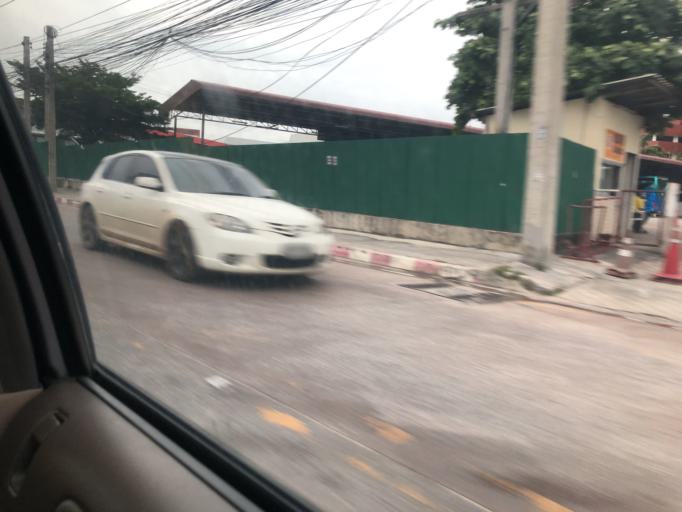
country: TH
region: Chon Buri
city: Phatthaya
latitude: 12.9485
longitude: 100.8915
